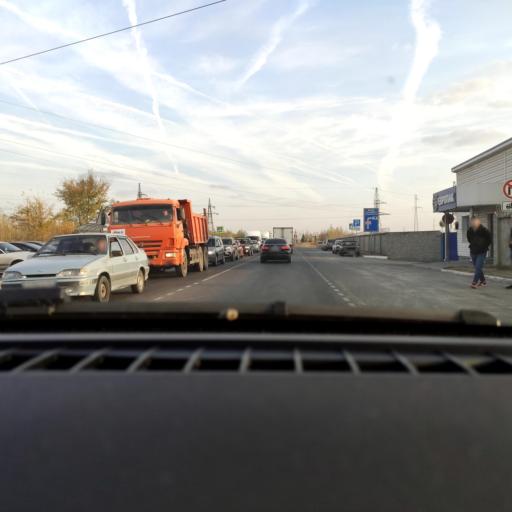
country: RU
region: Voronezj
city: Maslovka
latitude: 51.5893
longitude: 39.2515
